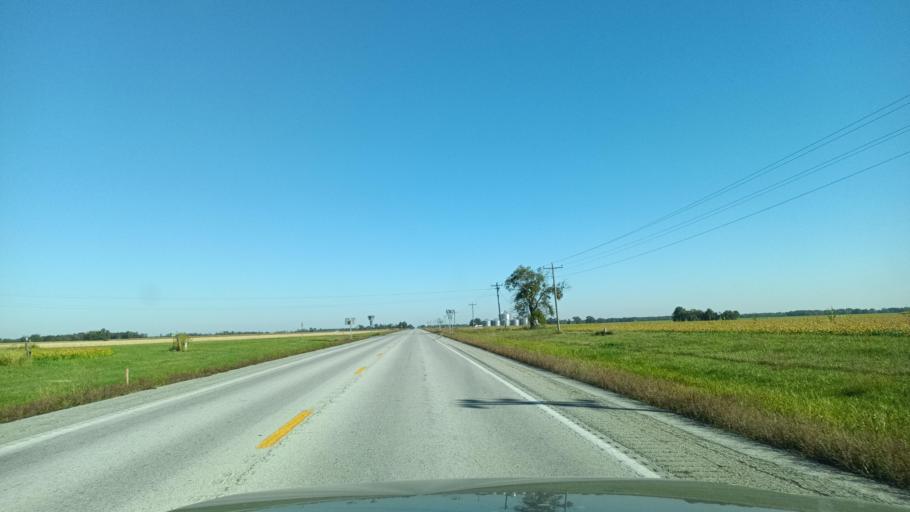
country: US
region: Missouri
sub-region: Audrain County
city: Vandalia
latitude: 39.3592
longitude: -91.6425
